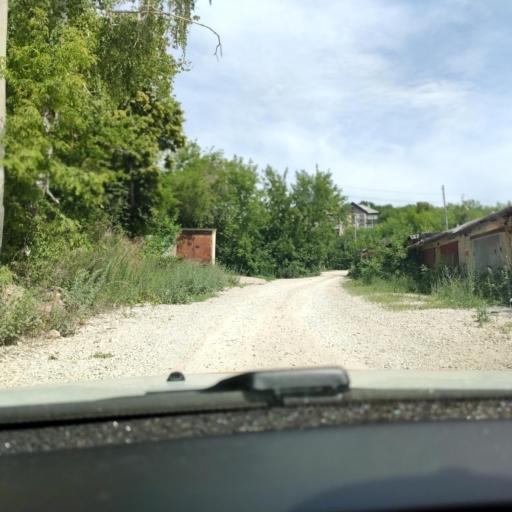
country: RU
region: Samara
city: Volzhskiy
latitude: 53.3420
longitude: 50.1999
